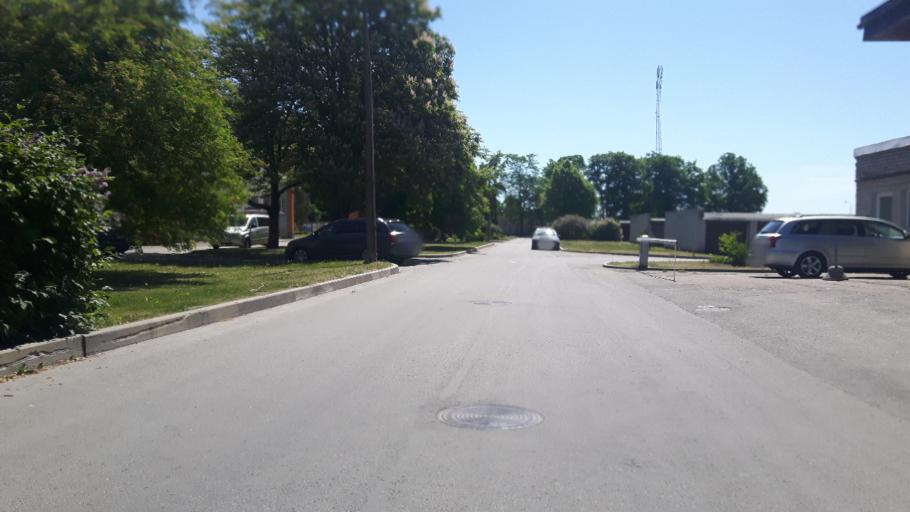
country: EE
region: Harju
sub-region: Saku vald
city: Saku
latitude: 59.2976
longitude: 24.6637
